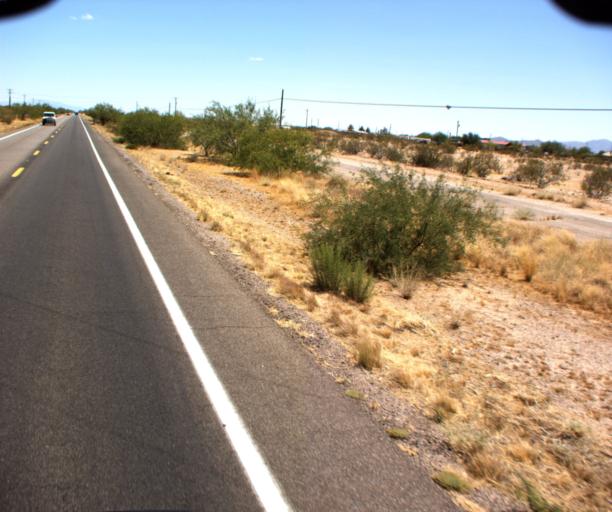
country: US
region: Arizona
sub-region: Pinal County
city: Florence
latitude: 32.9822
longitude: -111.3563
